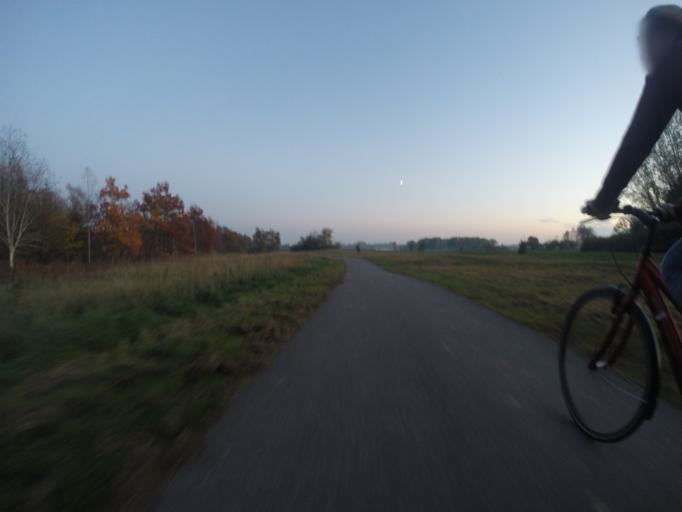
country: DK
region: Capital Region
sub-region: Vallensbaek Kommune
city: Vallensbaek
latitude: 55.6385
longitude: 12.3528
